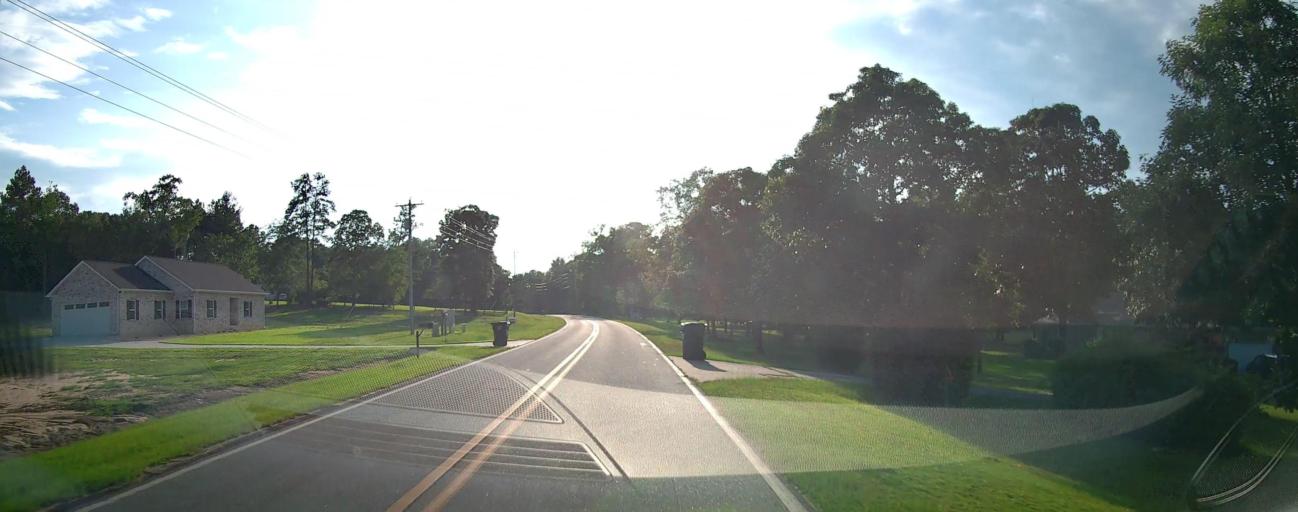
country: US
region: Georgia
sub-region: Peach County
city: Byron
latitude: 32.7052
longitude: -83.8273
